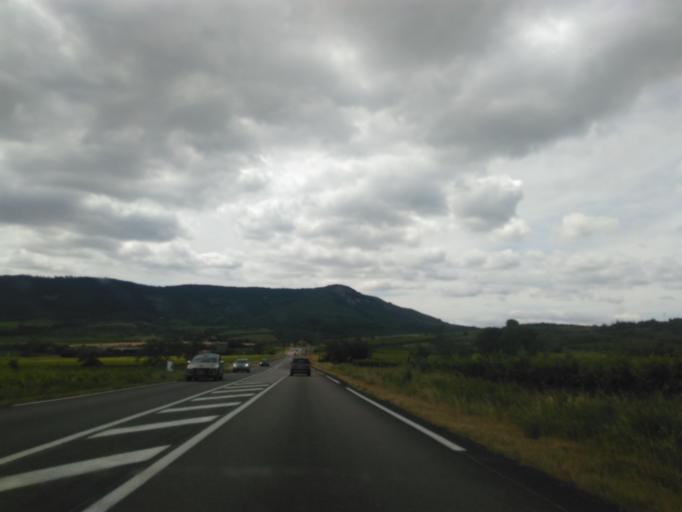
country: FR
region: Rhone-Alpes
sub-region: Departement de l'Ardeche
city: Alba-la-Romaine
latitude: 44.5667
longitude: 4.6010
